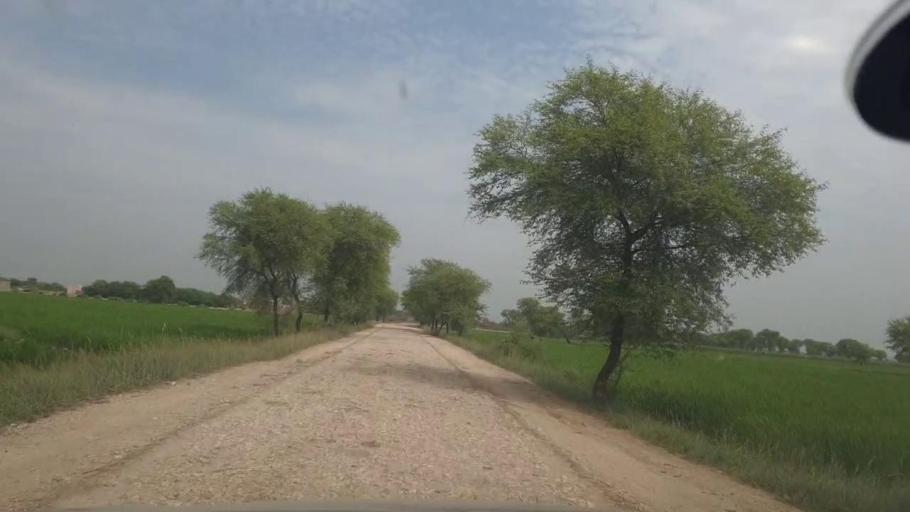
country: PK
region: Sindh
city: Jacobabad
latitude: 28.2494
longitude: 68.5424
